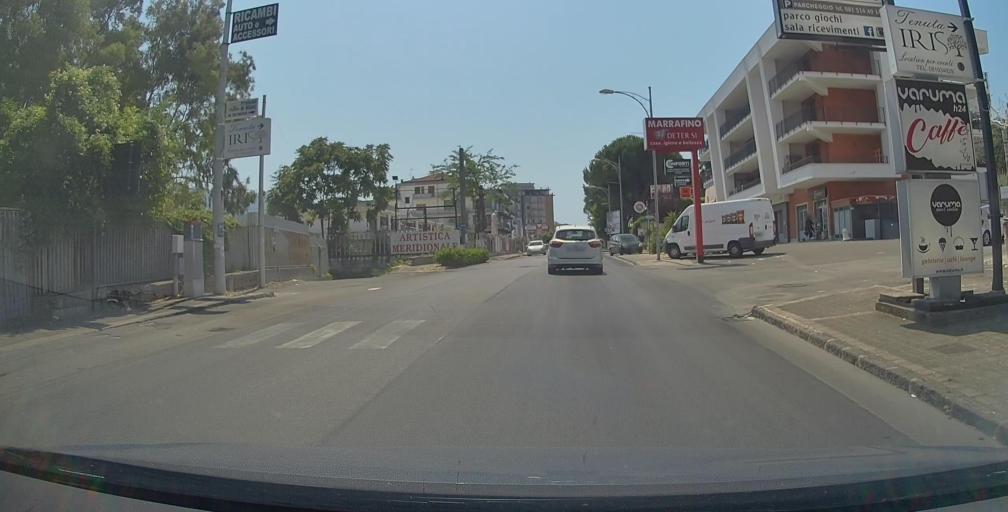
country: IT
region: Campania
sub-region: Provincia di Salerno
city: Nocera Superiore
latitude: 40.7320
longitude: 14.6868
